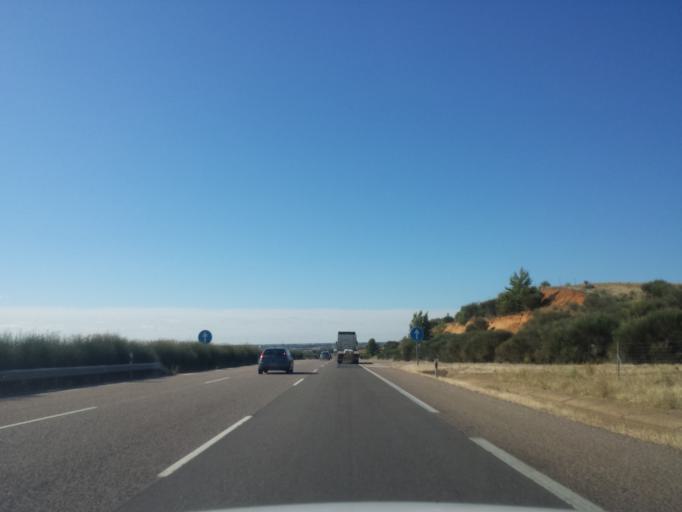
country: ES
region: Castille and Leon
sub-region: Provincia de Zamora
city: Benavente
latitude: 42.0333
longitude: -5.6719
